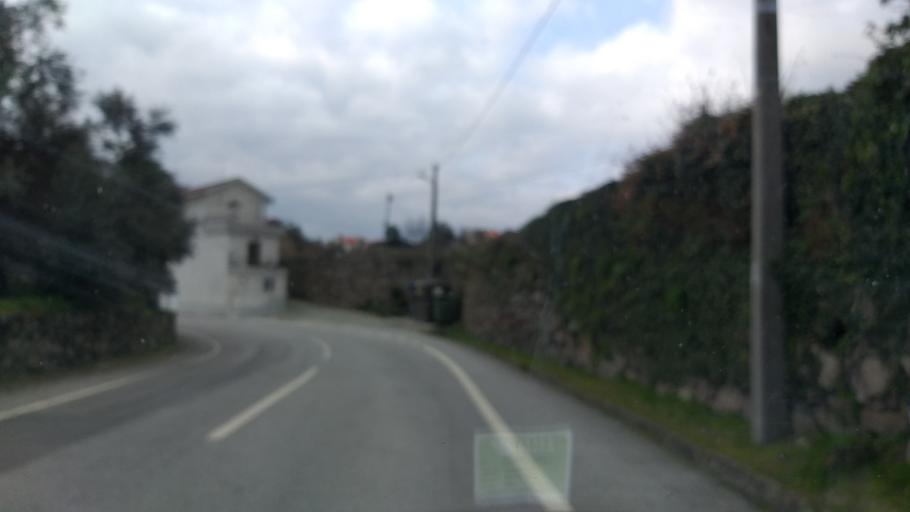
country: PT
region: Guarda
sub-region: Seia
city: Seia
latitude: 40.4759
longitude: -7.6320
